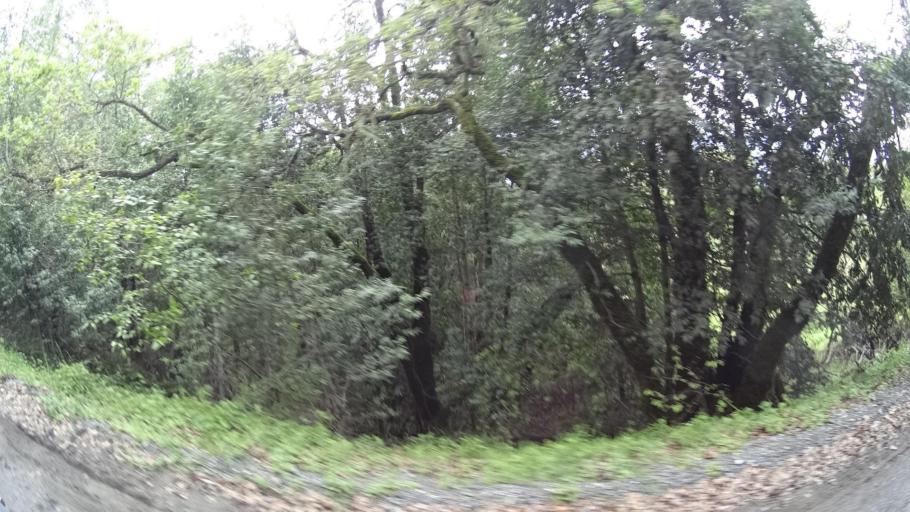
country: US
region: California
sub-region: Humboldt County
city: Blue Lake
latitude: 40.8587
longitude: -123.9124
